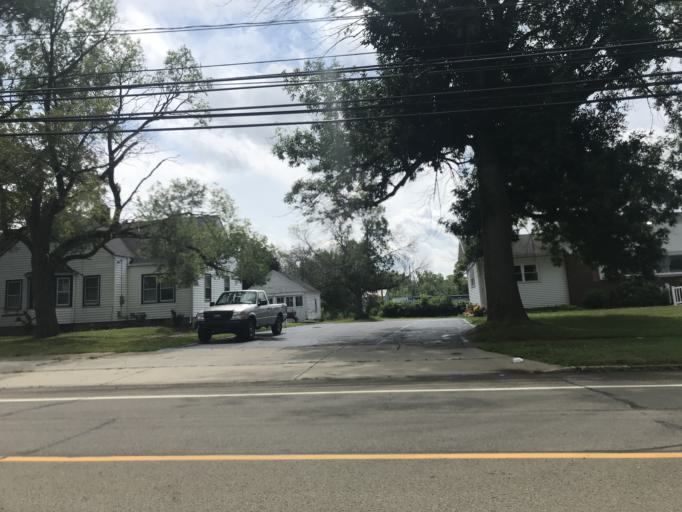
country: US
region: New York
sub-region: Chautauqua County
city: Dunkirk
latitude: 42.4853
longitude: -79.3489
